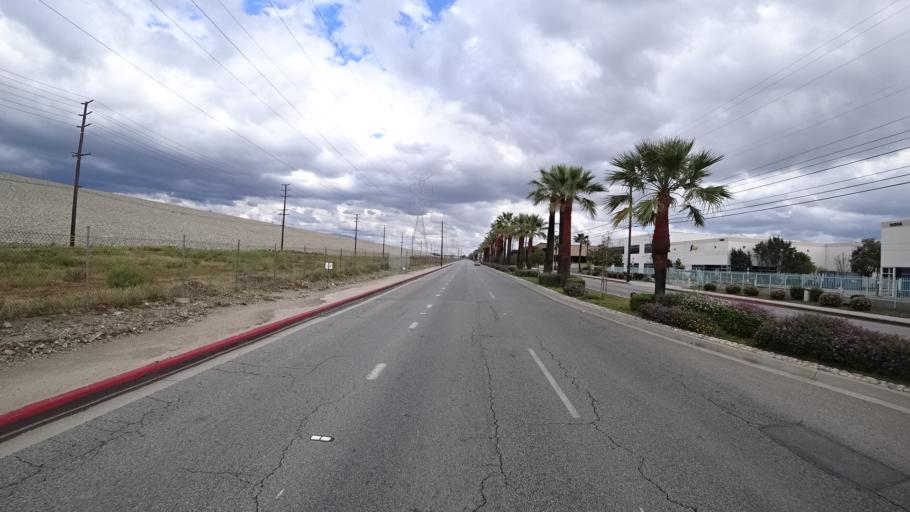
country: US
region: California
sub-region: Los Angeles County
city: Baldwin Park
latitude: 34.1069
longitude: -117.9583
